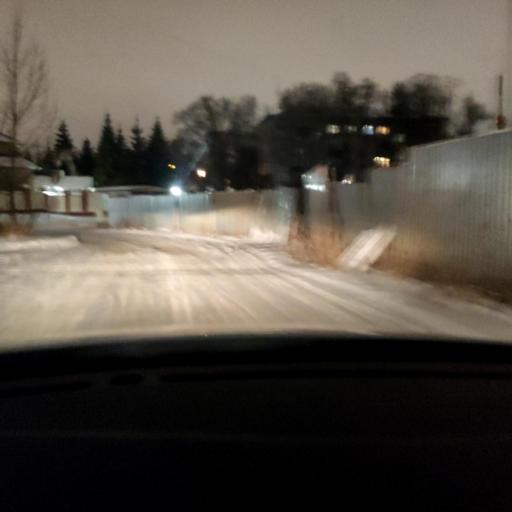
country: RU
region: Tatarstan
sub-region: Gorod Kazan'
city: Kazan
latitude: 55.7955
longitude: 49.1454
